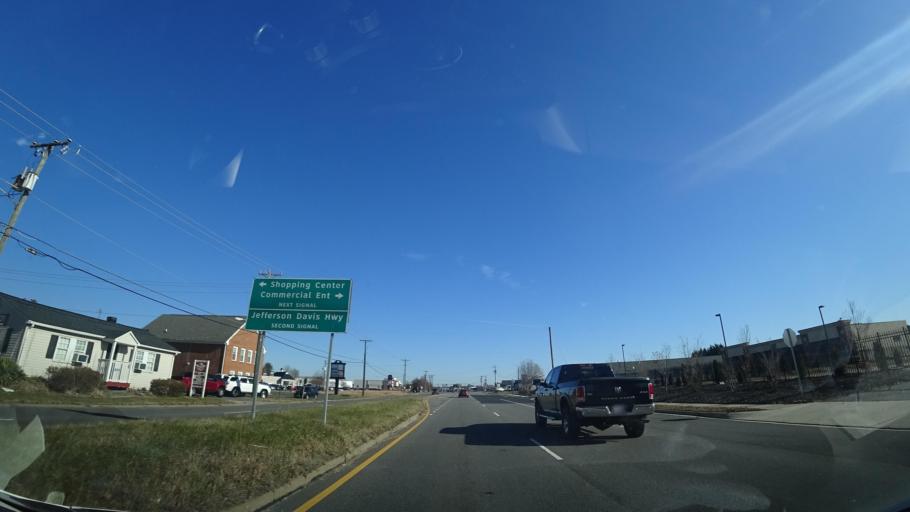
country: US
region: Virginia
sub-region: City of Fredericksburg
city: Fredericksburg
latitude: 38.2526
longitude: -77.5028
